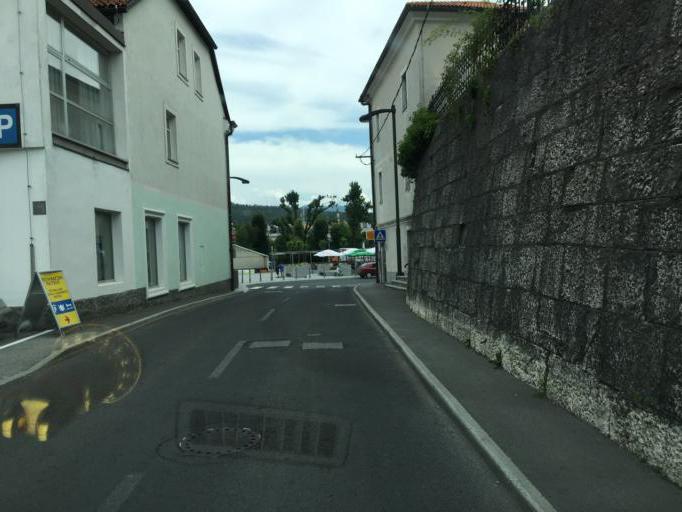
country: SI
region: Postojna
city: Postojna
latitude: 45.7756
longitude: 14.2122
